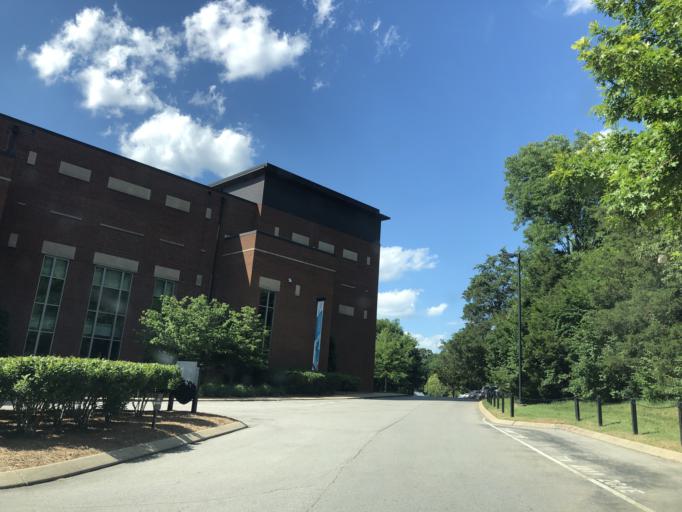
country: US
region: Tennessee
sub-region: Davidson County
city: Belle Meade
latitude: 36.0568
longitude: -86.9189
